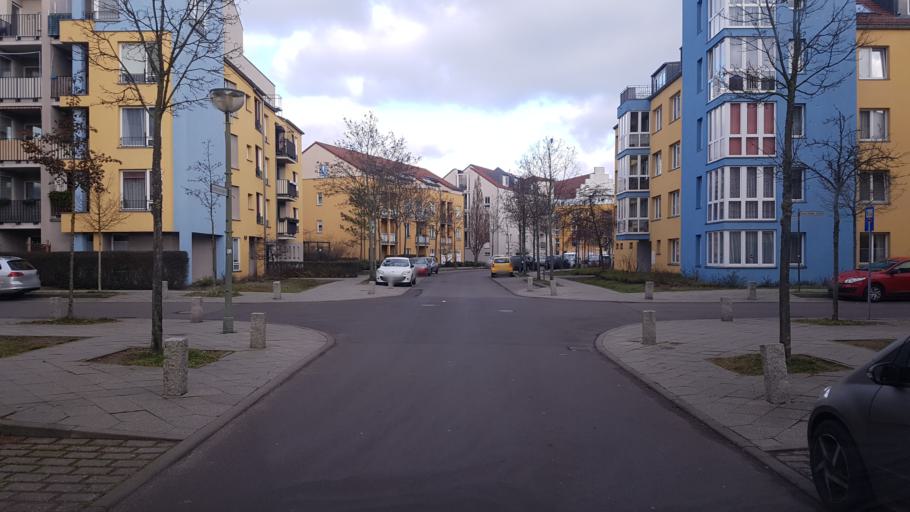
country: DE
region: Berlin
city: Wannsee
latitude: 52.3633
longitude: 13.1346
